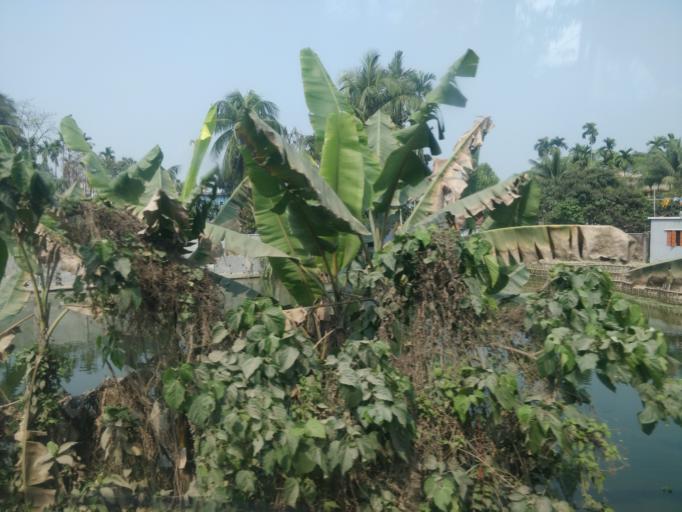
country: BD
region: Sylhet
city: Habiganj
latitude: 24.3643
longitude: 91.4185
